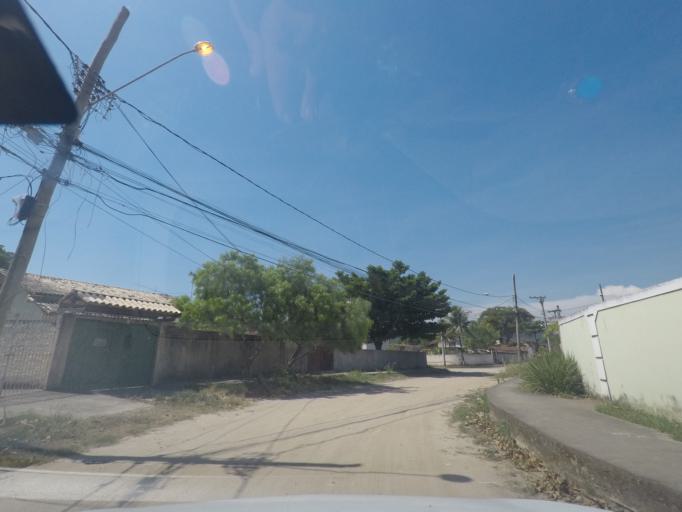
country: BR
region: Rio de Janeiro
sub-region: Niteroi
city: Niteroi
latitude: -22.9458
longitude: -43.0261
